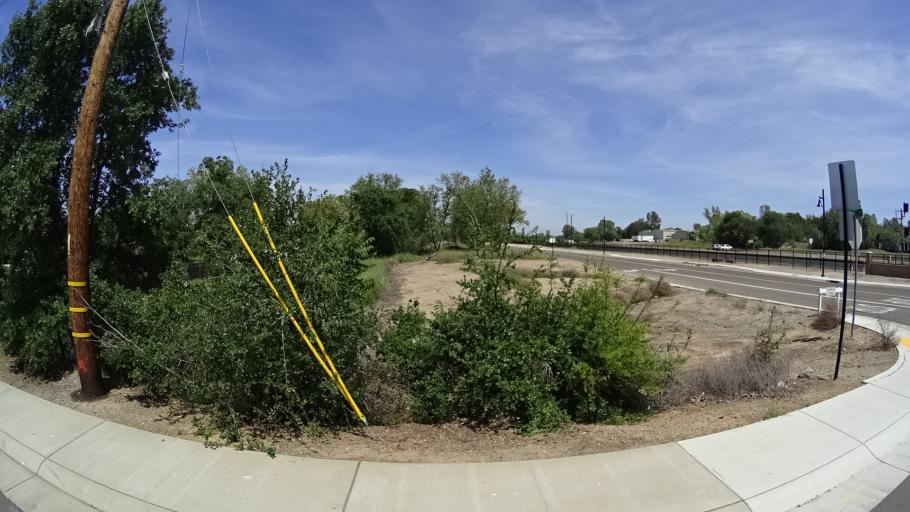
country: US
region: California
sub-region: Placer County
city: Rocklin
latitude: 38.7867
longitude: -121.2416
